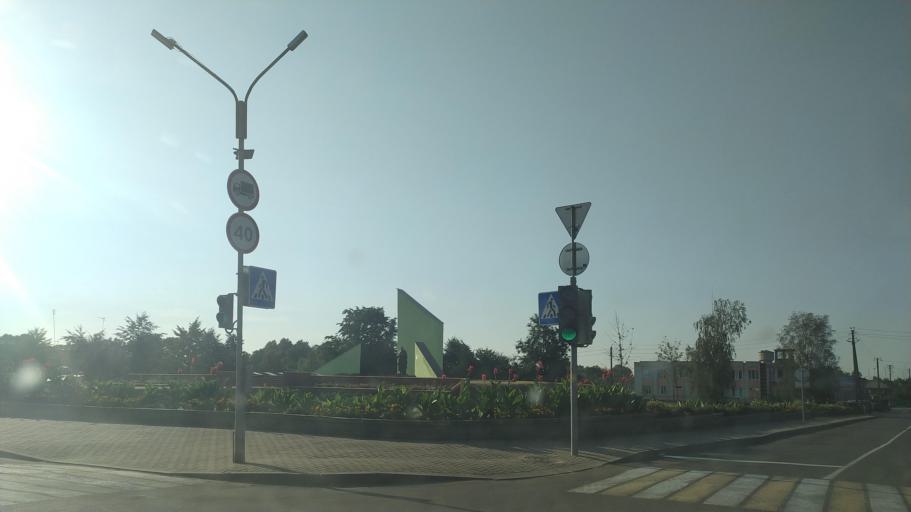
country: BY
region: Brest
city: Drahichyn
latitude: 52.1868
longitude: 25.1447
